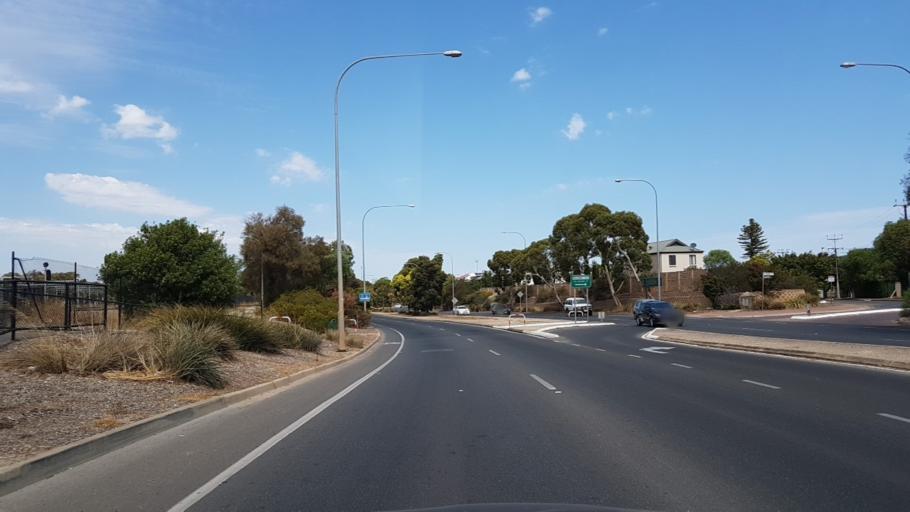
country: AU
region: South Australia
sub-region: City of West Torrens
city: Thebarton
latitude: -34.9242
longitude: 138.5795
